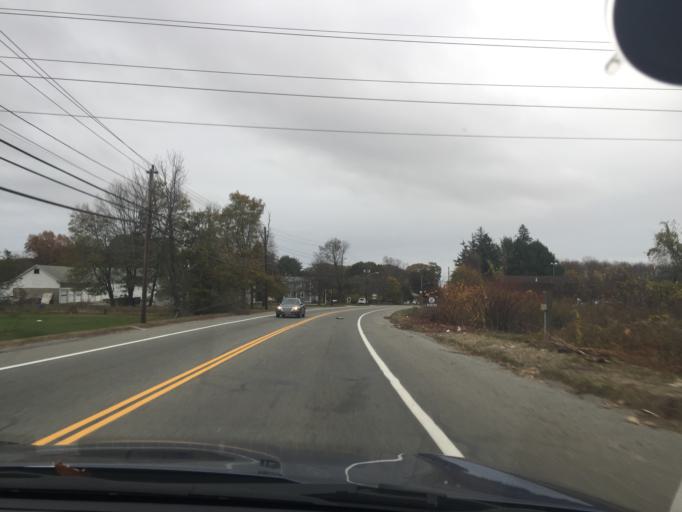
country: US
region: Rhode Island
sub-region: Providence County
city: Johnston
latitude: 41.7898
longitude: -71.5229
